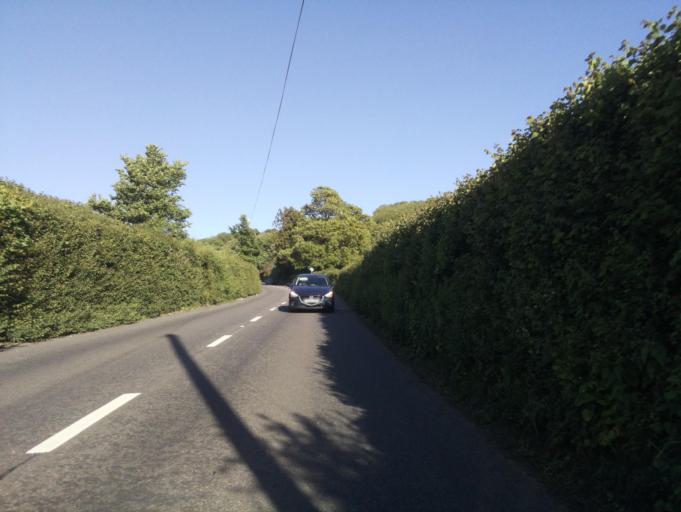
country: GB
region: England
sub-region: Devon
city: Sidmouth
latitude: 50.7004
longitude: -3.2153
